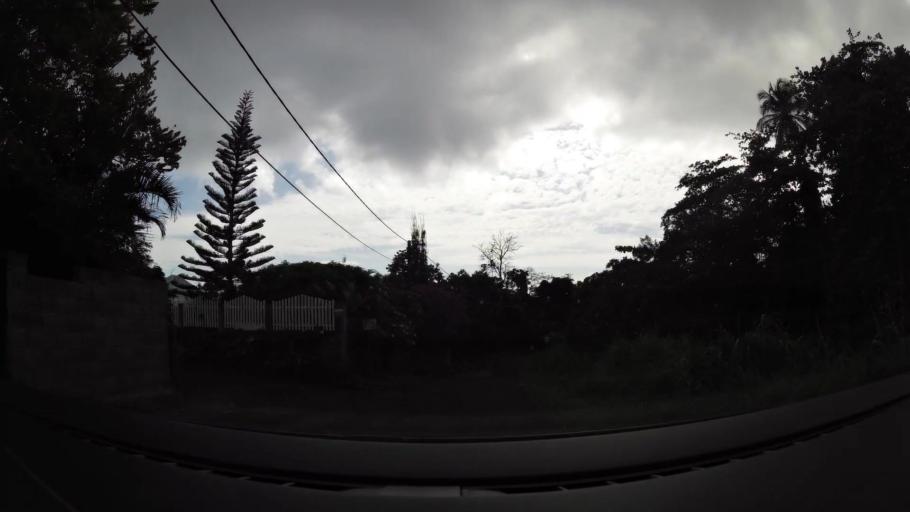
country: GP
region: Guadeloupe
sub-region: Guadeloupe
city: Trois-Rivieres
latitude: 15.9812
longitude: -61.6367
